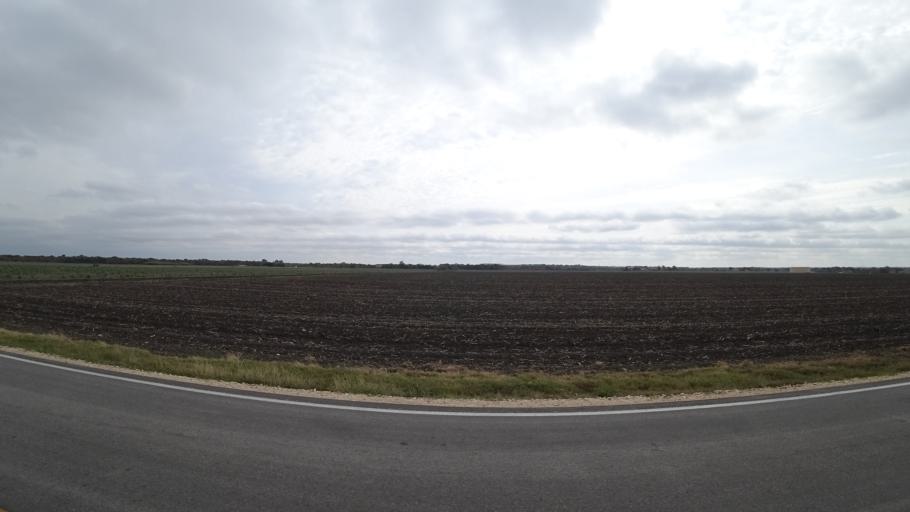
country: US
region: Texas
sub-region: Travis County
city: Manor
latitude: 30.3935
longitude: -97.5501
